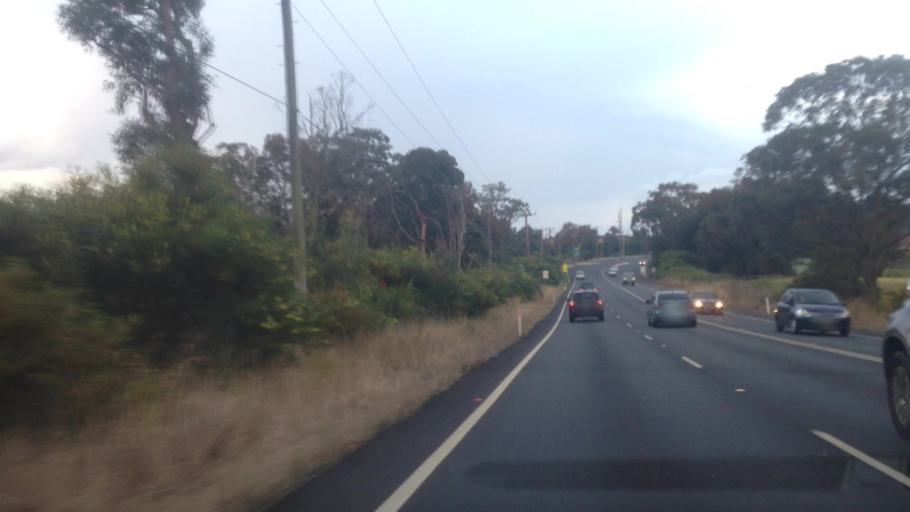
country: AU
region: New South Wales
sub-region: Wyong Shire
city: Kanwal
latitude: -33.2553
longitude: 151.4871
